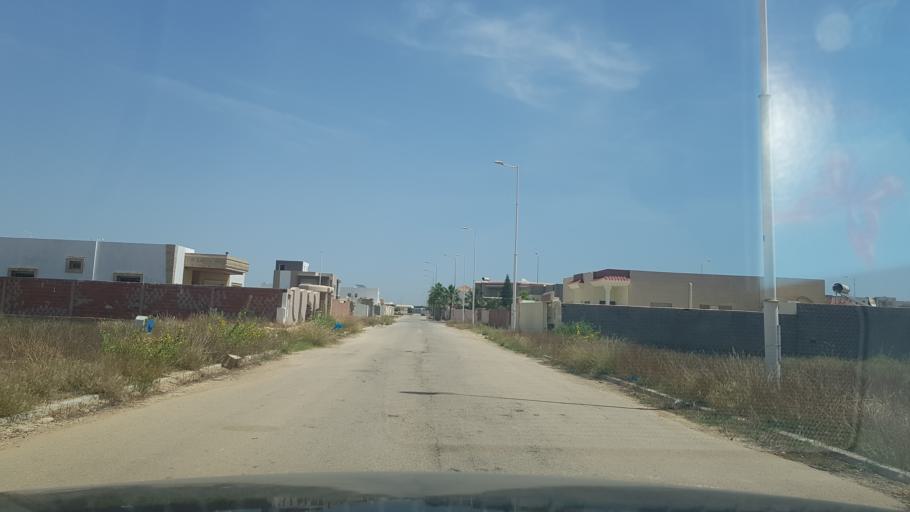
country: TN
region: Safaqis
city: Al Qarmadah
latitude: 34.8344
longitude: 10.7561
